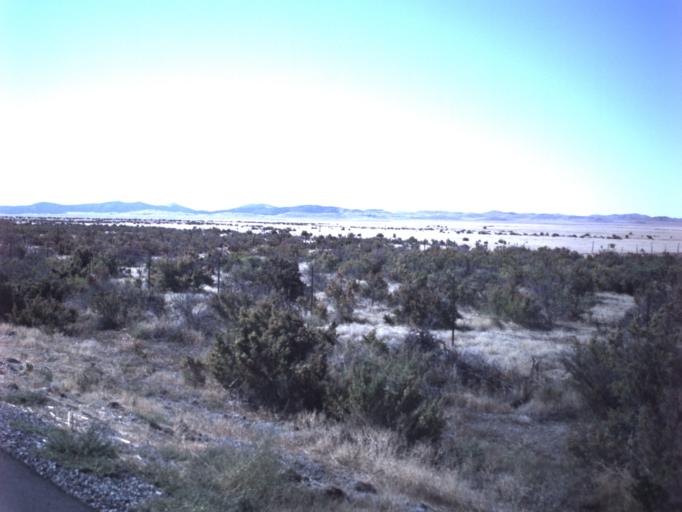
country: US
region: Utah
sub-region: Tooele County
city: Grantsville
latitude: 40.3472
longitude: -112.7452
